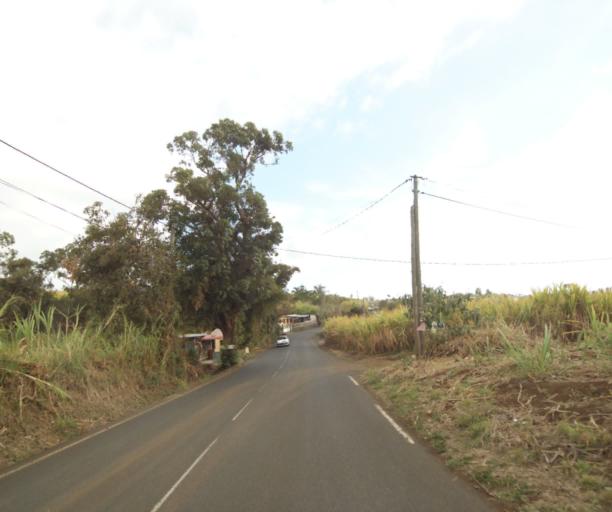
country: RE
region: Reunion
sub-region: Reunion
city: Trois-Bassins
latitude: -21.0707
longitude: 55.2779
